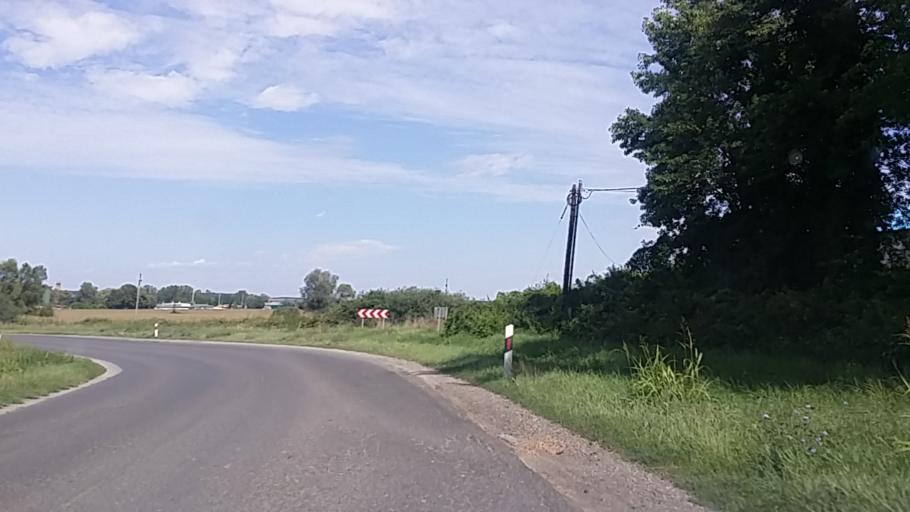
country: HU
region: Baranya
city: Sasd
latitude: 46.2497
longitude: 18.1194
